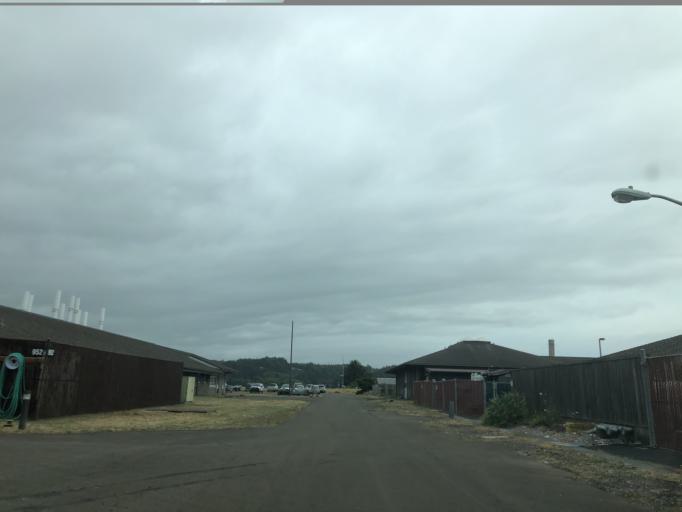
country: US
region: Oregon
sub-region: Lincoln County
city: Newport
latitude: 44.6222
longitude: -124.0435
